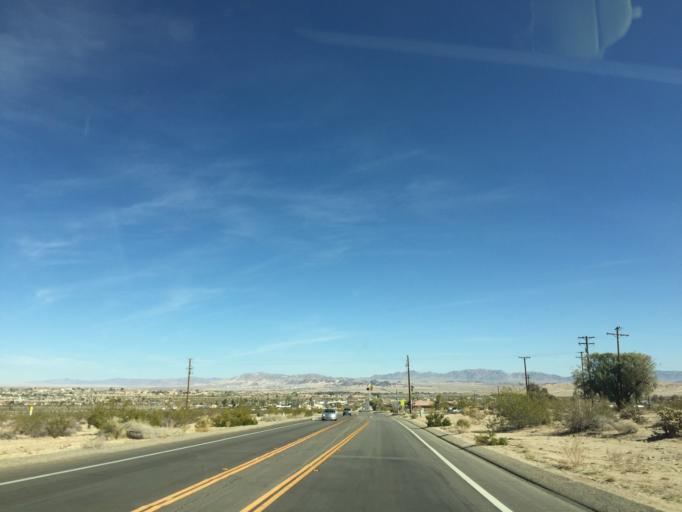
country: US
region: California
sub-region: San Bernardino County
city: Twentynine Palms
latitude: 34.1197
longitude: -116.0366
